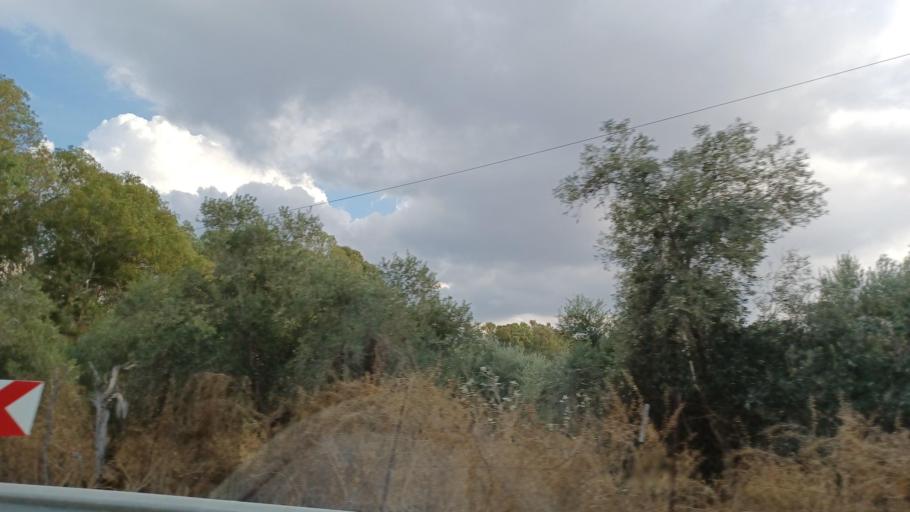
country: CY
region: Pafos
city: Polis
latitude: 35.0542
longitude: 32.4543
